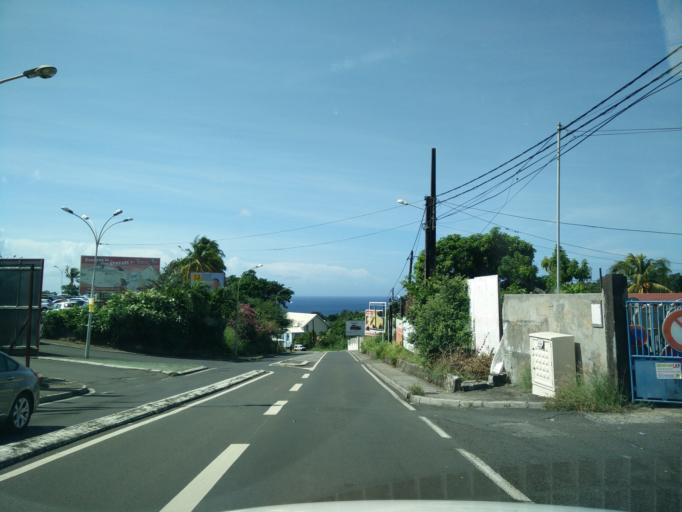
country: GP
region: Guadeloupe
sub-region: Guadeloupe
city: Basse-Terre
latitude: 16.0010
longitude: -61.7190
